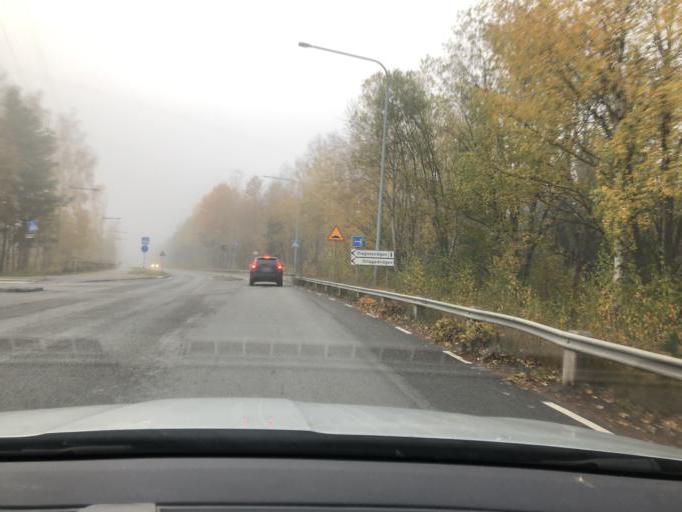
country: SE
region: Stockholm
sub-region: Huddinge Kommun
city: Huddinge
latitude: 59.2251
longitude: 17.9464
